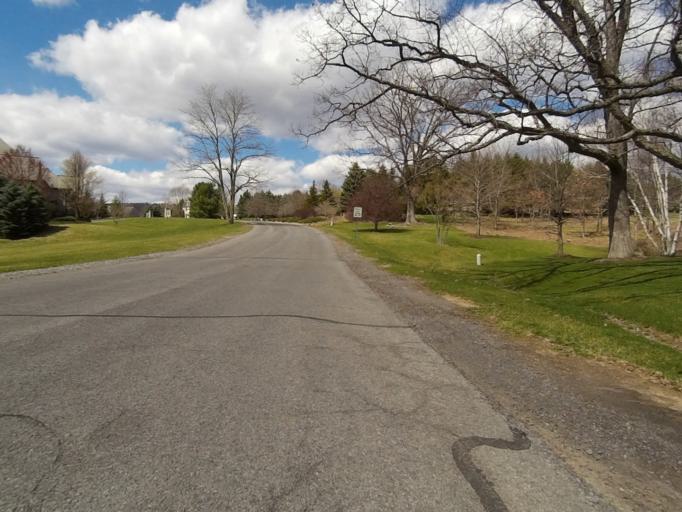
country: US
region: Pennsylvania
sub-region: Centre County
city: Park Forest Village
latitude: 40.8188
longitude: -77.9599
